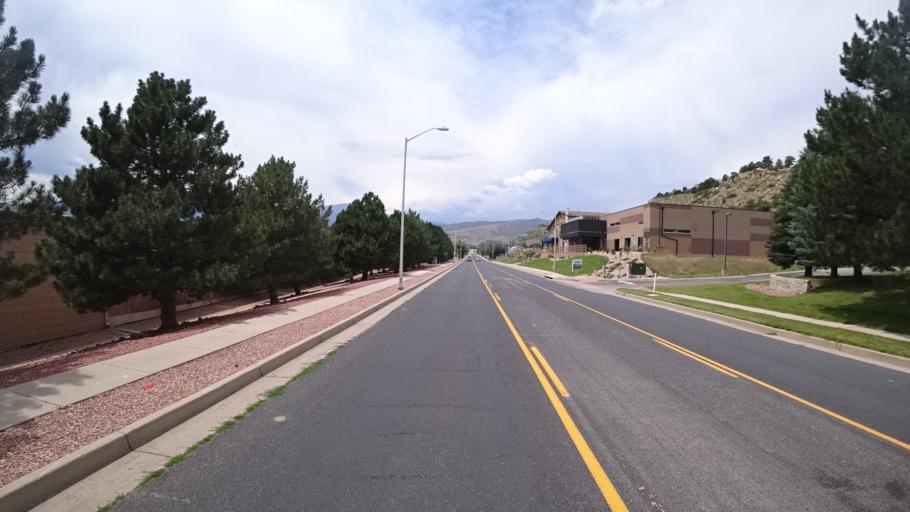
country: US
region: Colorado
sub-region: El Paso County
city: Colorado Springs
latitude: 38.9007
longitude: -104.8337
